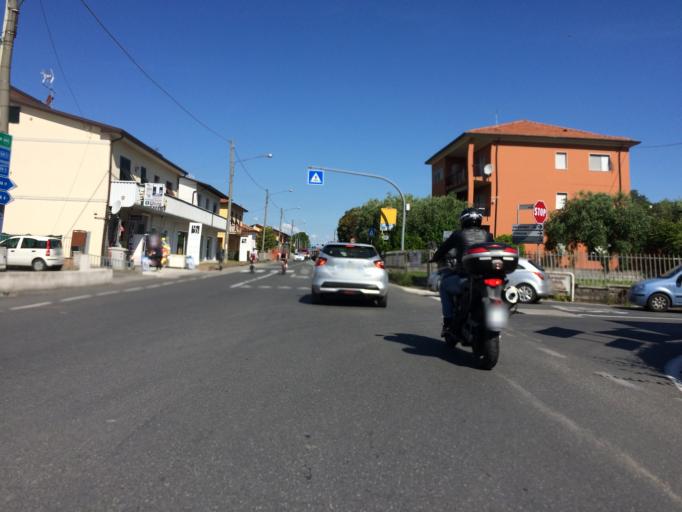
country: IT
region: Liguria
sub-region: Provincia di La Spezia
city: Casano-Dogana-Isola
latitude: 44.0707
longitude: 10.0240
